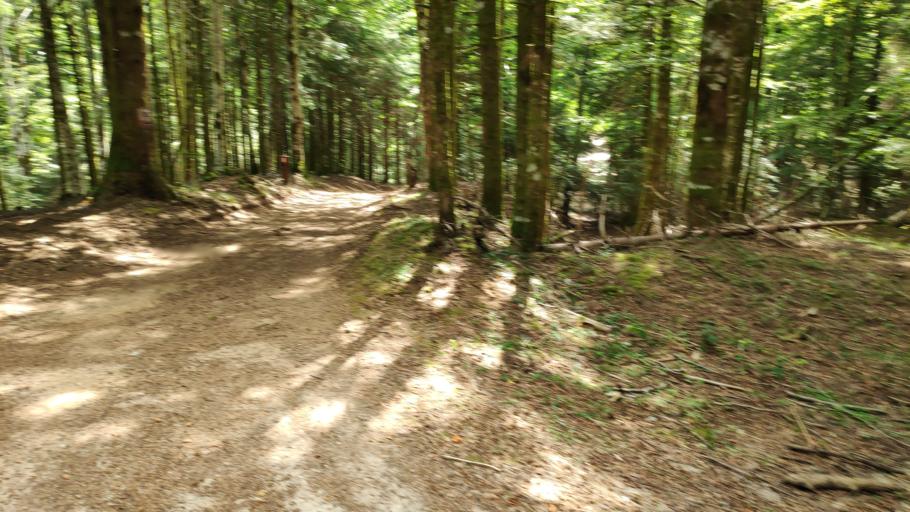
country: IT
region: Calabria
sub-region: Provincia di Vibo-Valentia
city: Serra San Bruno
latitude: 38.5425
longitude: 16.3599
